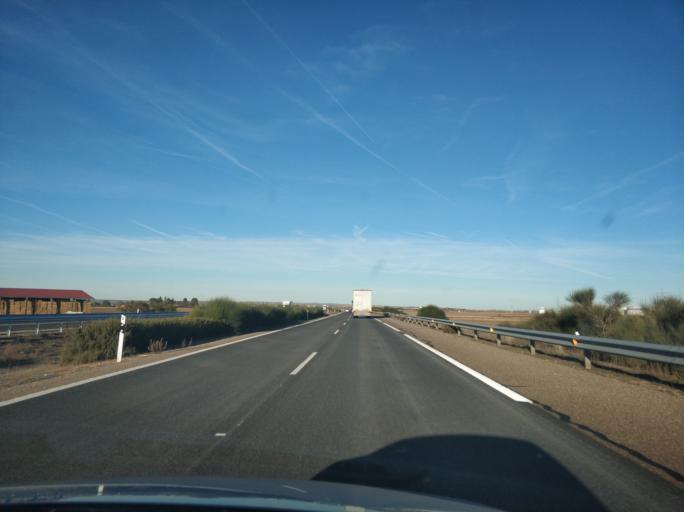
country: ES
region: Castille and Leon
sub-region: Provincia de Salamanca
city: Castellanos de Moriscos
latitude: 41.0185
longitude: -5.5819
